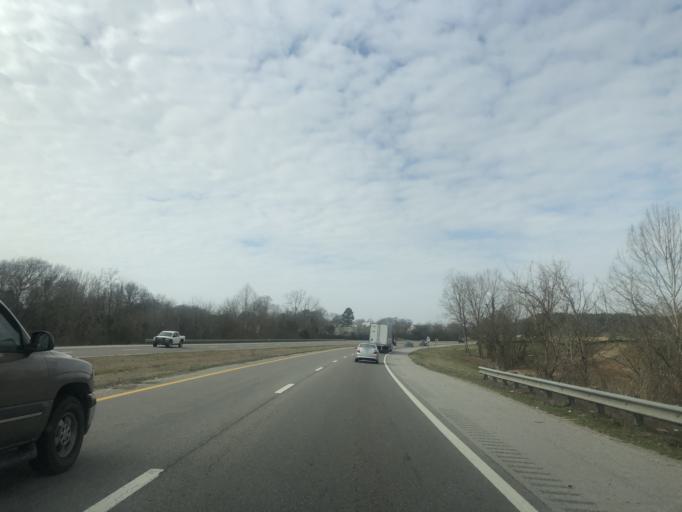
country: US
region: Tennessee
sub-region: Maury County
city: Columbia
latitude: 35.6377
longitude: -87.0365
